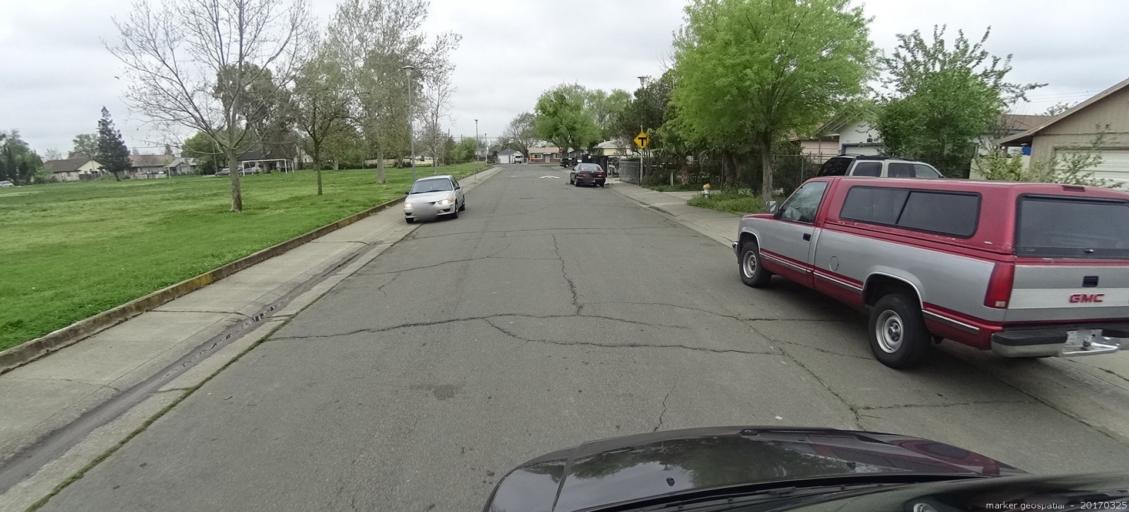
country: US
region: California
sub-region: Sacramento County
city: Florin
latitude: 38.5222
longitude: -121.4131
